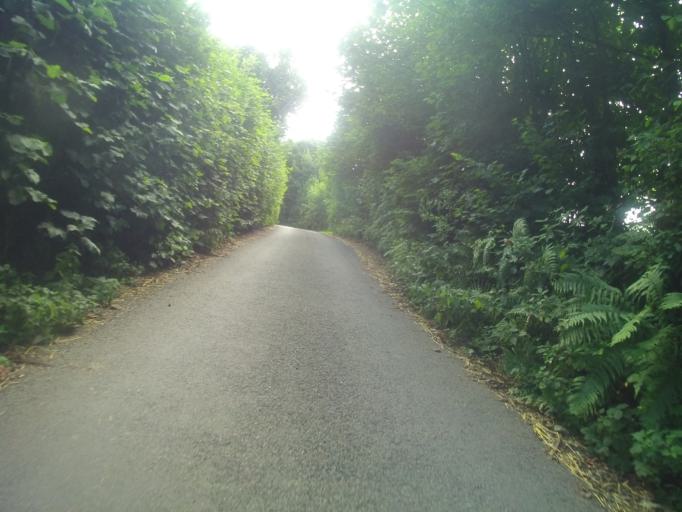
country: GB
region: England
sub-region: Devon
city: Buckfastleigh
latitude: 50.5037
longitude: -3.8223
